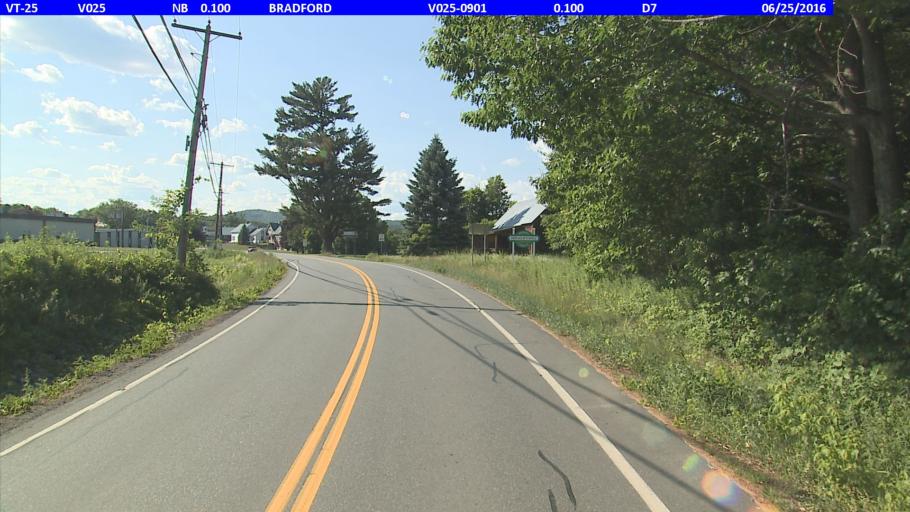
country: US
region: New Hampshire
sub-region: Grafton County
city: Haverhill
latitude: 43.9790
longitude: -72.1137
